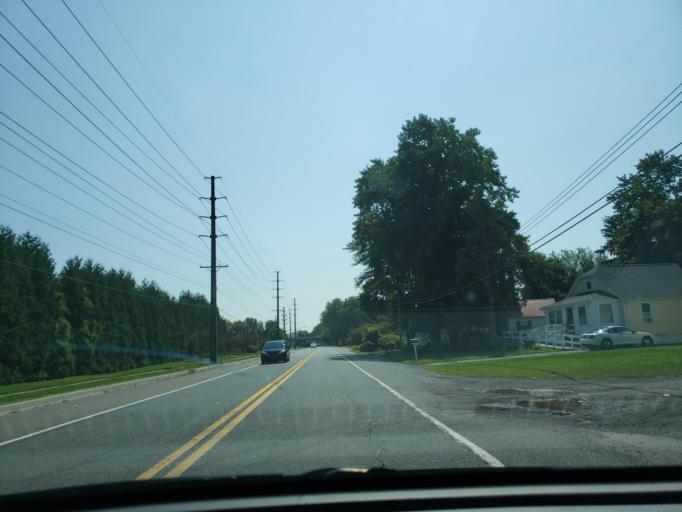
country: US
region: Delaware
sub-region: Kent County
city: Dover
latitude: 39.1665
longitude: -75.4978
